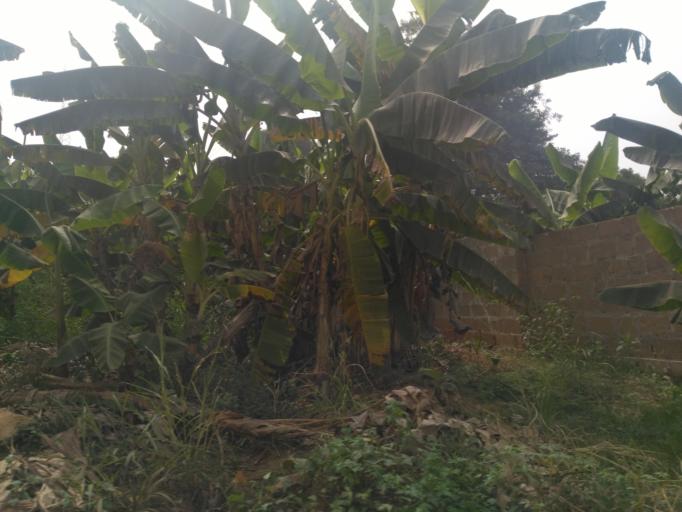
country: GH
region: Ashanti
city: Kumasi
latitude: 6.6790
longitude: -1.6205
